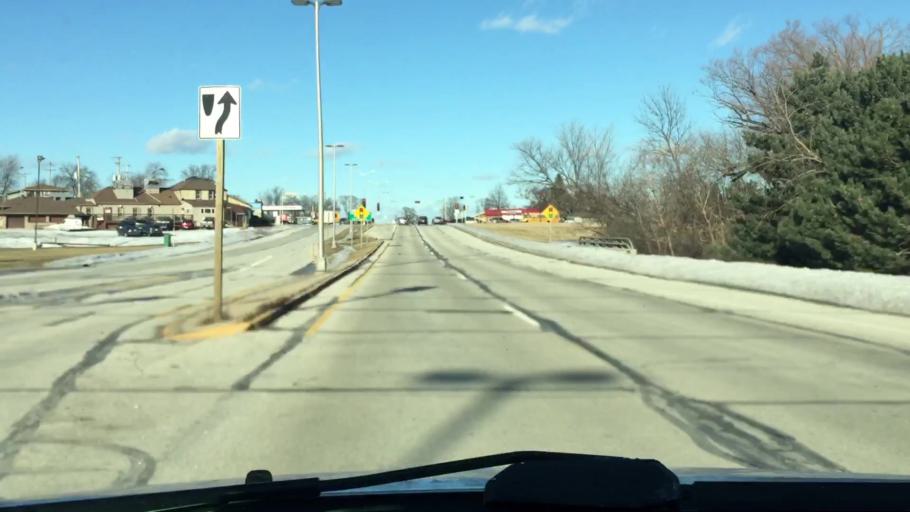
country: US
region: Wisconsin
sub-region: Milwaukee County
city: West Milwaukee
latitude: 42.9725
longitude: -87.9582
